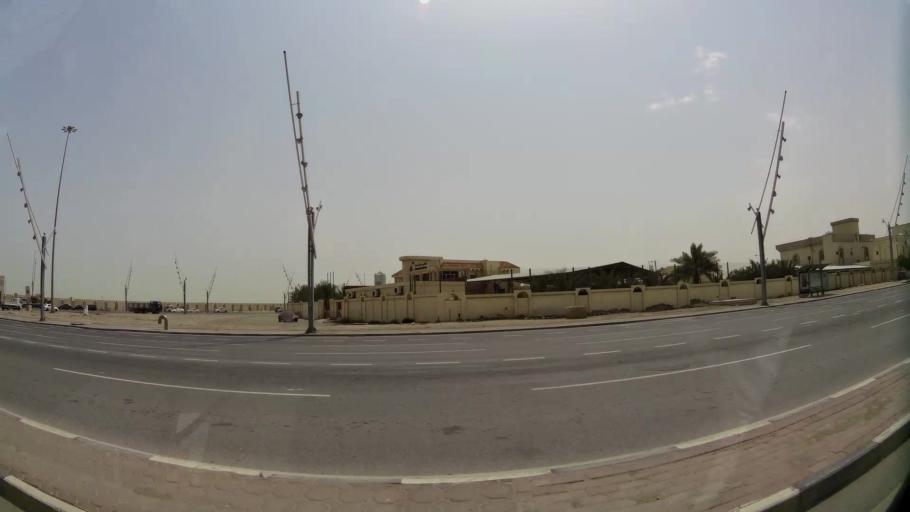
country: QA
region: Baladiyat ar Rayyan
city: Ar Rayyan
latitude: 25.2516
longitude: 51.4300
